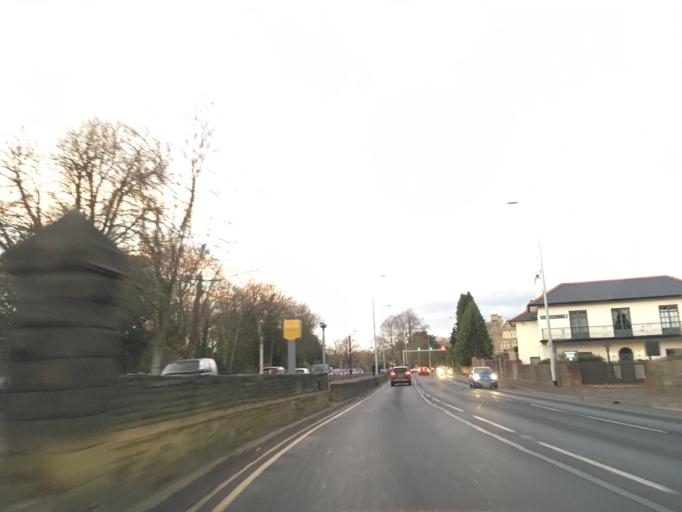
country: GB
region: Wales
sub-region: Cardiff
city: Cardiff
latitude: 51.4894
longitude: -3.1869
